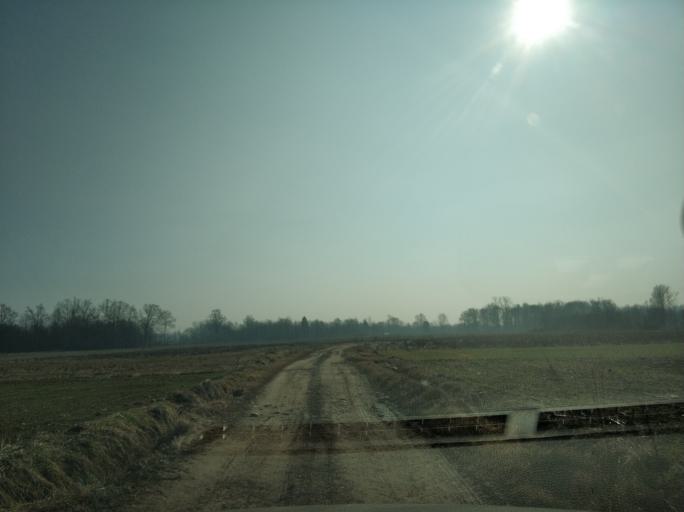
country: IT
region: Piedmont
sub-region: Provincia di Torino
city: Lombardore
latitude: 45.2484
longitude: 7.7351
